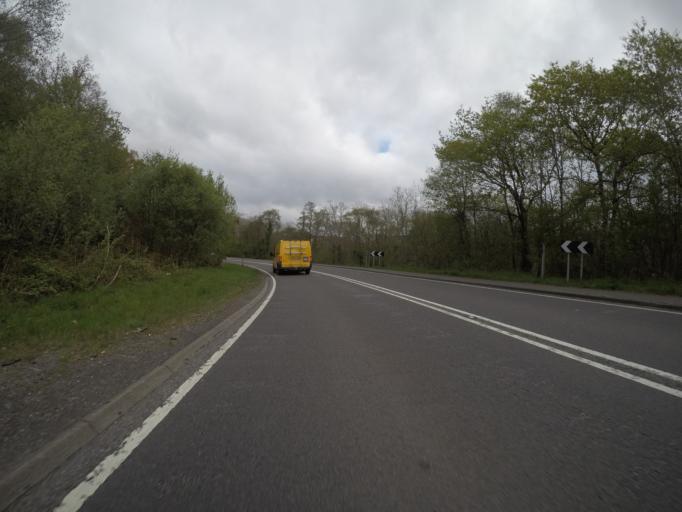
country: GB
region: Scotland
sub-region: Highland
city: Fort William
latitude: 56.7143
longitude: -5.2267
